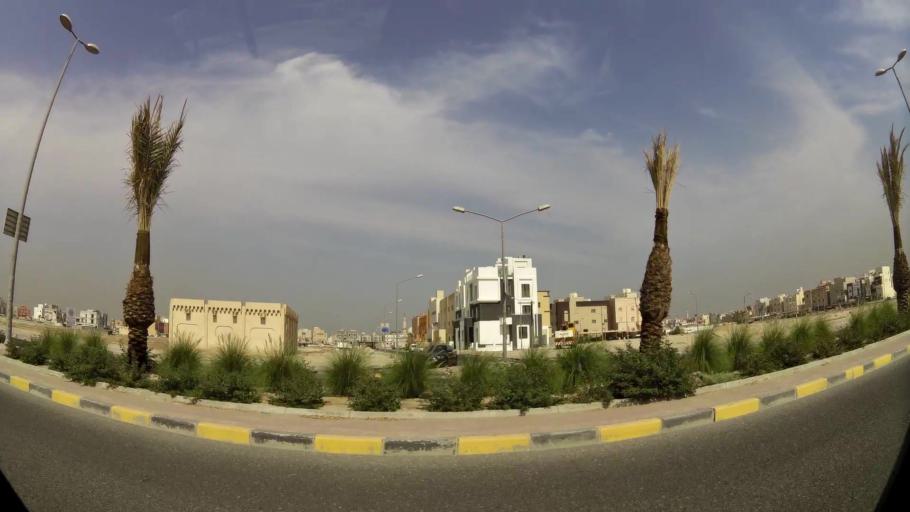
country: KW
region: Al Farwaniyah
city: Janub as Surrah
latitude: 29.2903
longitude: 48.0008
